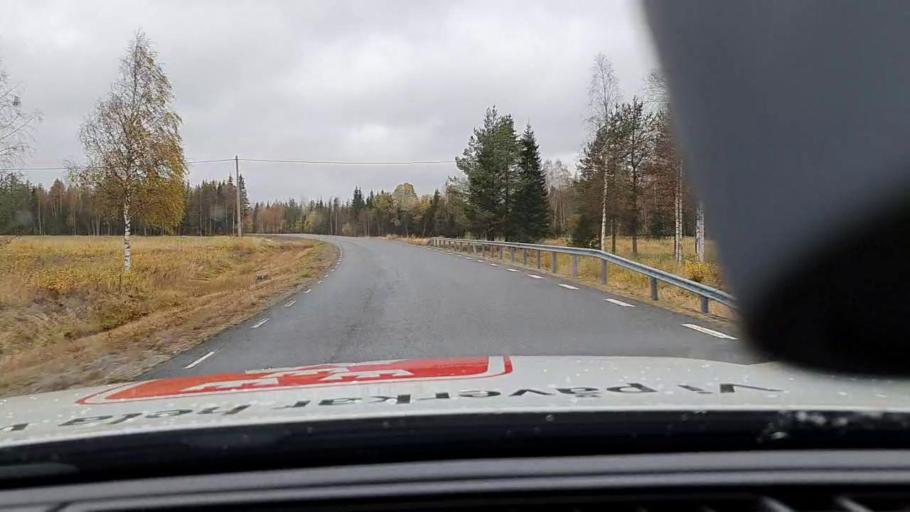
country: SE
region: Norrbotten
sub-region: Haparanda Kommun
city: Haparanda
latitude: 65.9330
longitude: 23.8149
